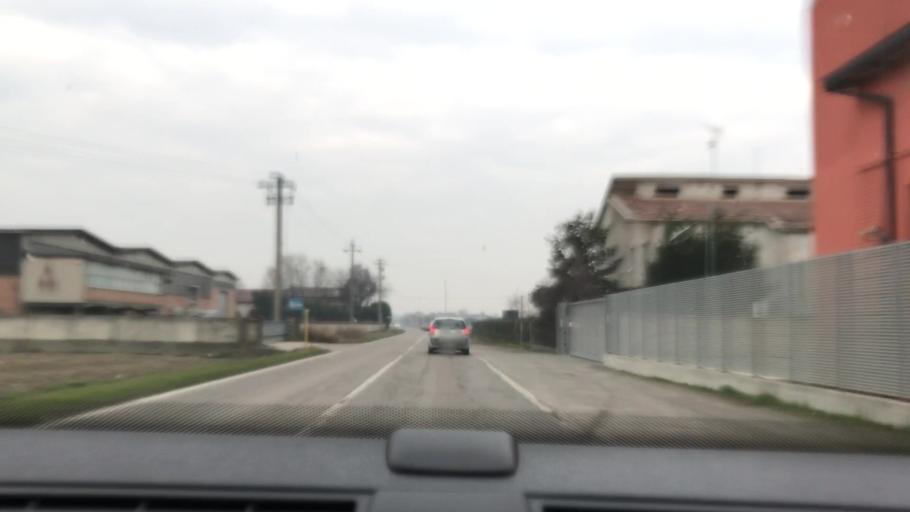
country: IT
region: Lombardy
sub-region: Provincia di Mantova
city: Dosolo
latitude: 44.9444
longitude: 10.6272
